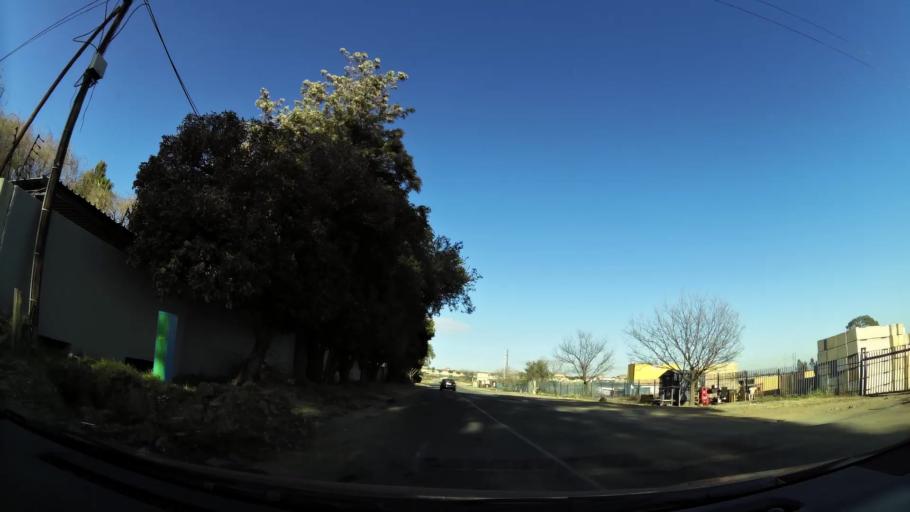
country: ZA
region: Gauteng
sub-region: City of Johannesburg Metropolitan Municipality
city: Midrand
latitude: -26.0379
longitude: 28.1466
